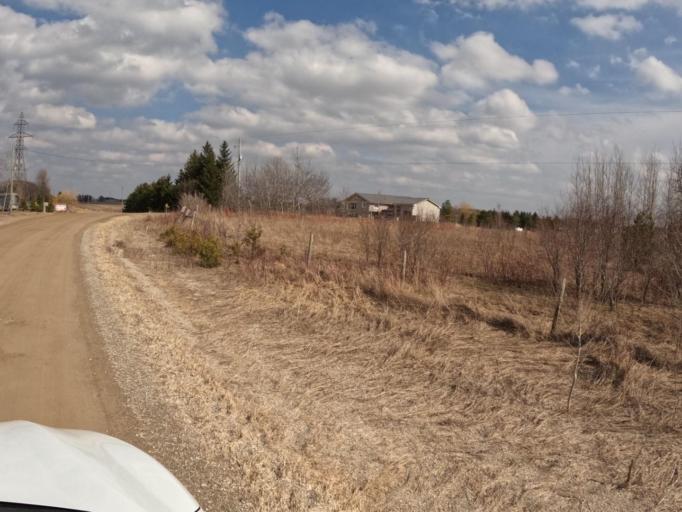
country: CA
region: Ontario
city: Shelburne
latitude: 43.9611
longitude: -80.3082
